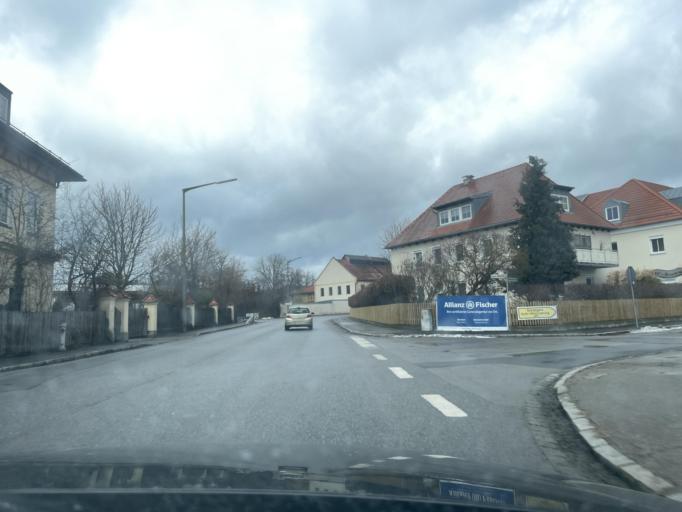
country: DE
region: Bavaria
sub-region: Upper Palatinate
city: Furth im Wald
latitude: 49.3080
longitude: 12.8347
